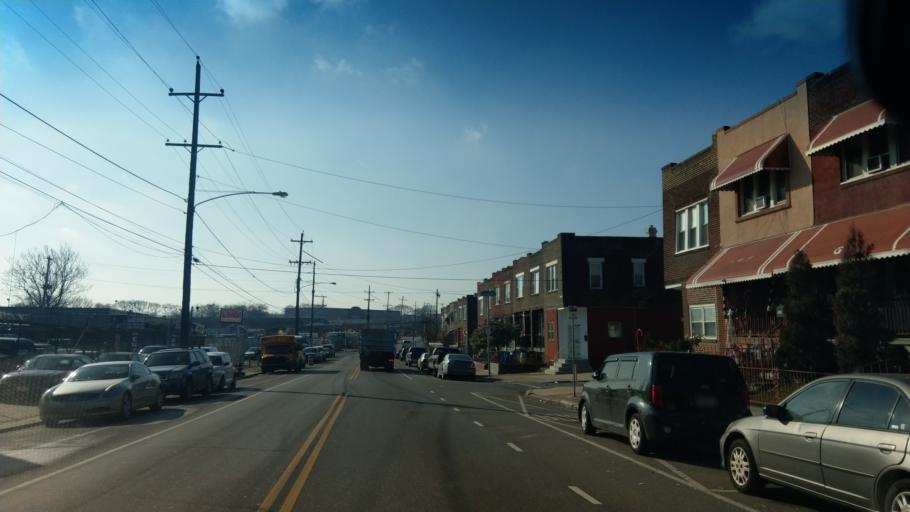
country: US
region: Pennsylvania
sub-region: Montgomery County
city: Rockledge
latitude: 40.0199
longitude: -75.1267
